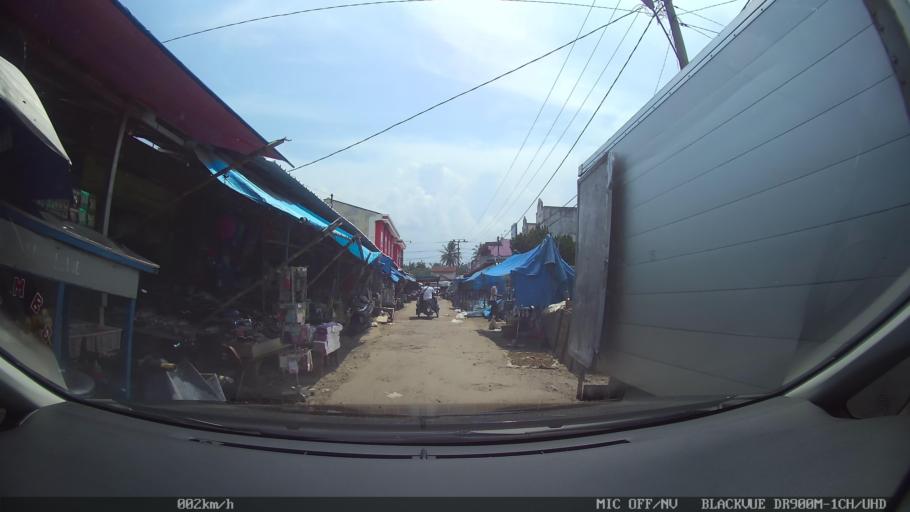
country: ID
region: Lampung
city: Natar
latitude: -5.3175
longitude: 105.1986
